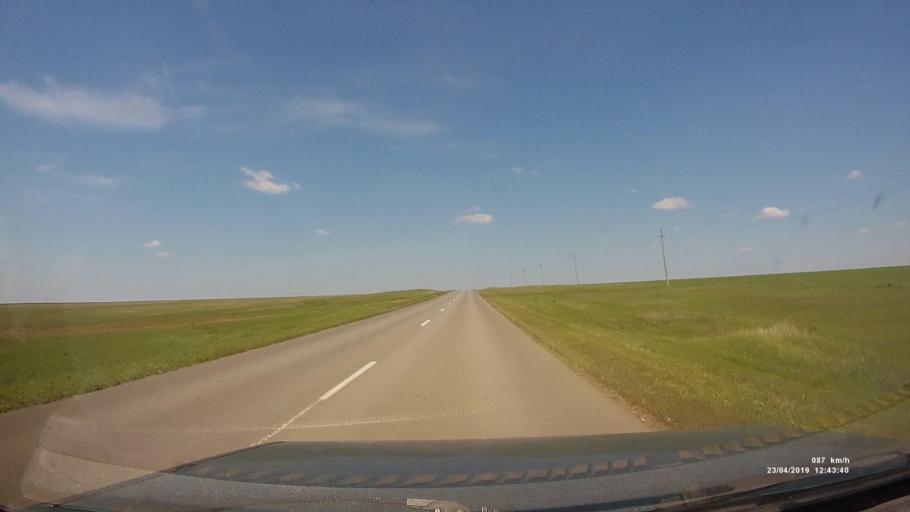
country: RU
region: Kalmykiya
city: Yashalta
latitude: 46.4669
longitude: 42.6502
